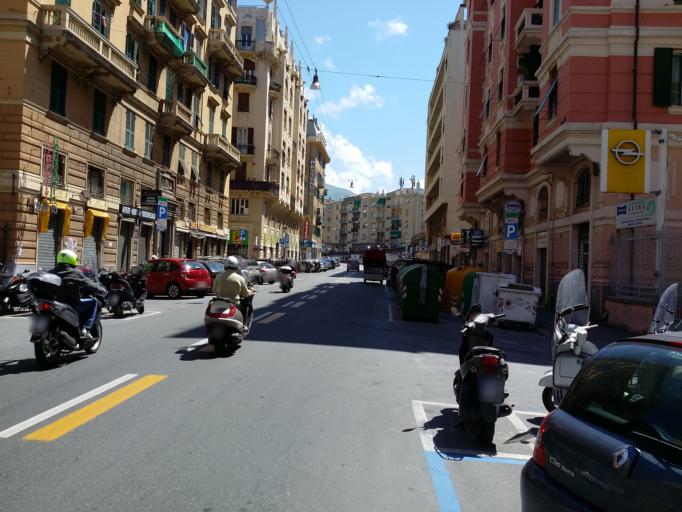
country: IT
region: Liguria
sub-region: Provincia di Genova
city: Genoa
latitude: 44.4065
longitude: 8.9578
